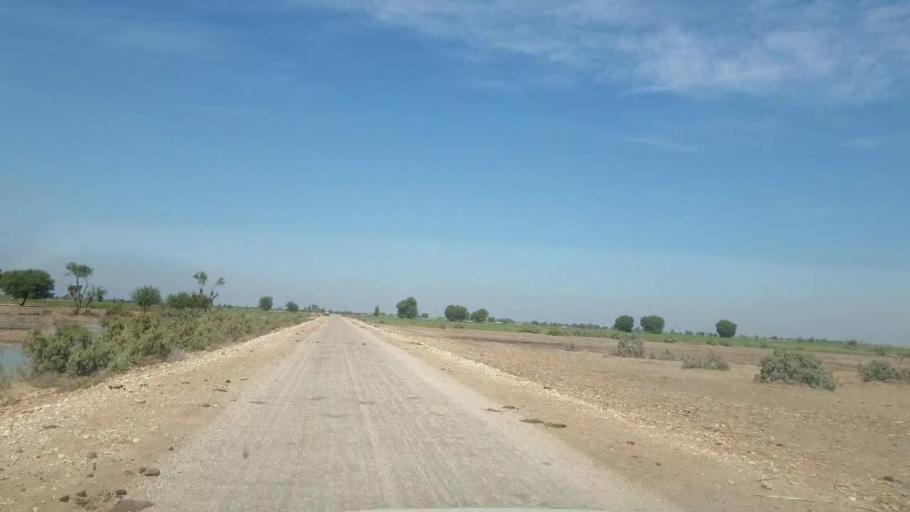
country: PK
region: Sindh
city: Mirpur Khas
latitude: 25.6427
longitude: 69.1938
